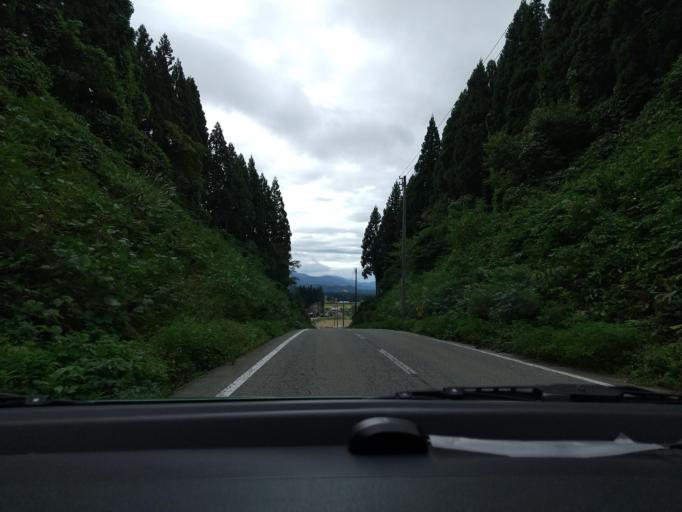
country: JP
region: Akita
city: Kakunodatemachi
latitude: 39.5410
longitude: 140.6414
